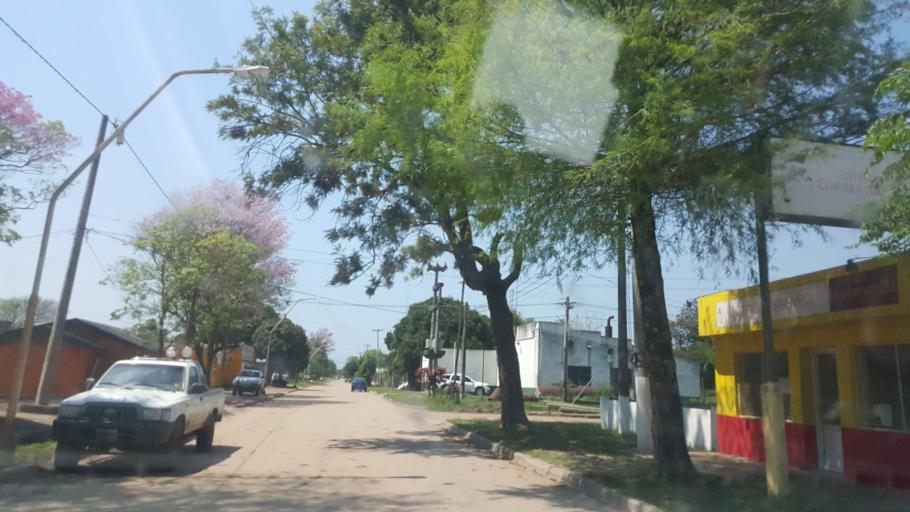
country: AR
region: Corrientes
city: Ita Ibate
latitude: -27.4249
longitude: -57.3347
